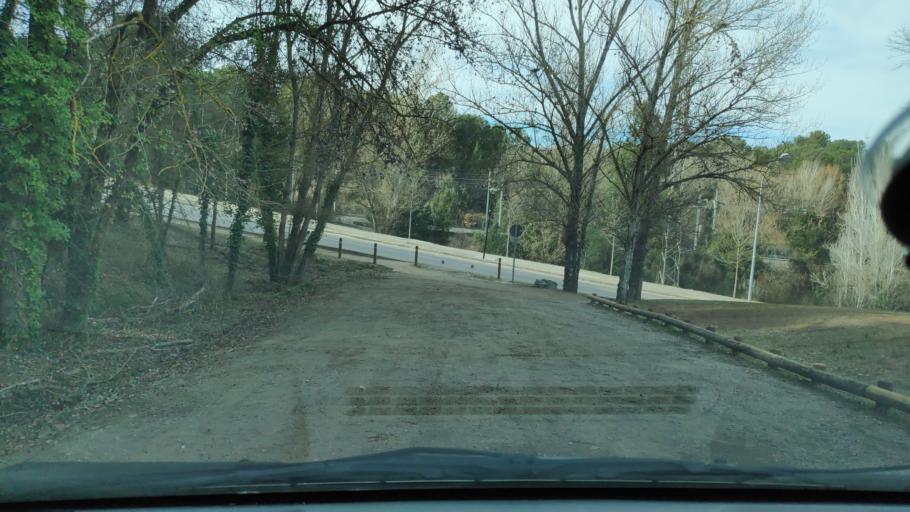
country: ES
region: Catalonia
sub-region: Provincia de Barcelona
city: Barbera del Valles
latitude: 41.5013
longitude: 2.1019
